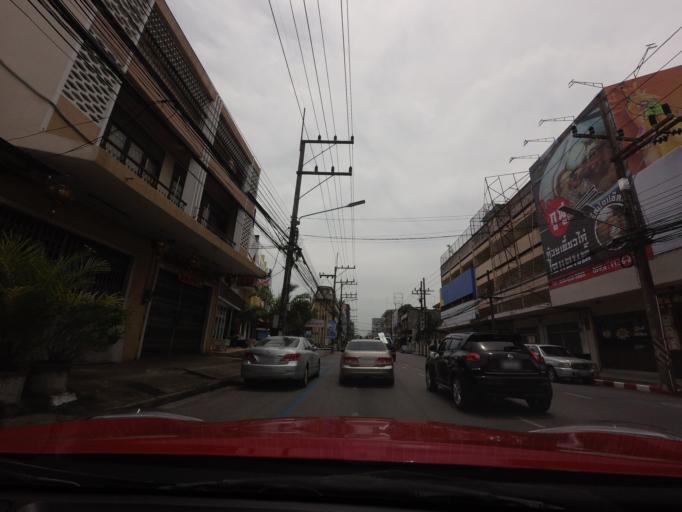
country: TH
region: Songkhla
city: Hat Yai
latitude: 6.9980
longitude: 100.4746
